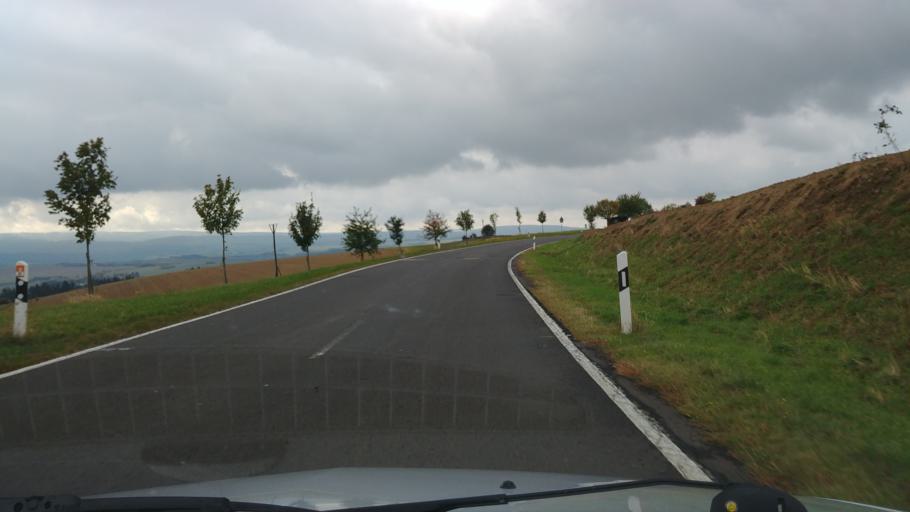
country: DE
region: Rheinland-Pfalz
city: Etgert
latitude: 49.8164
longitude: 7.0393
